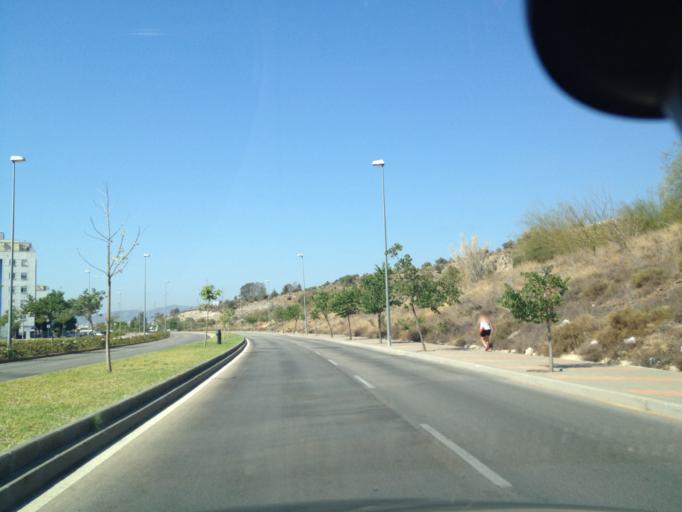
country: ES
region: Andalusia
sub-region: Provincia de Malaga
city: Malaga
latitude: 36.7267
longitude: -4.4809
